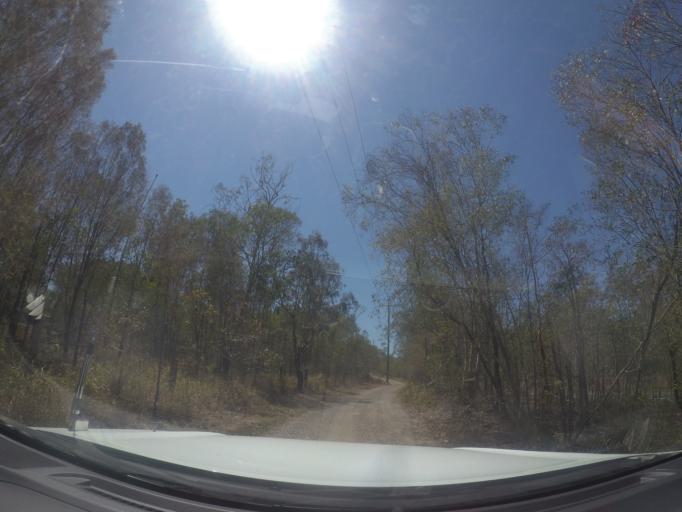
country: AU
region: Queensland
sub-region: Logan
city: North Maclean
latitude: -27.8062
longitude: 153.0488
